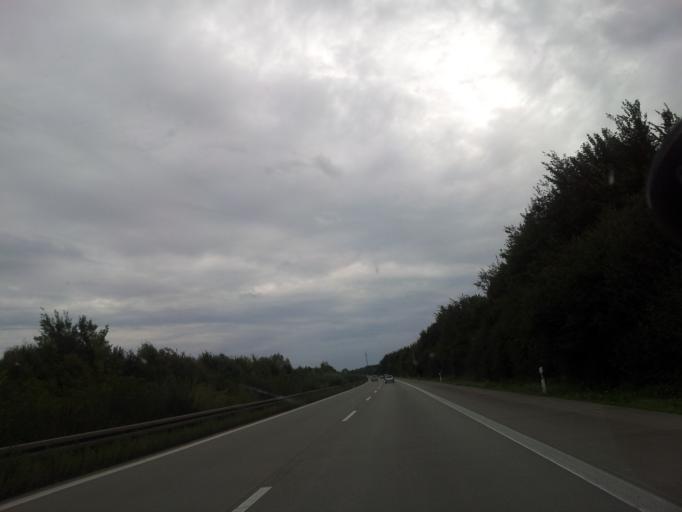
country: DE
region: Saxony-Anhalt
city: Hohendodeleben
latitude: 52.1167
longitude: 11.5284
